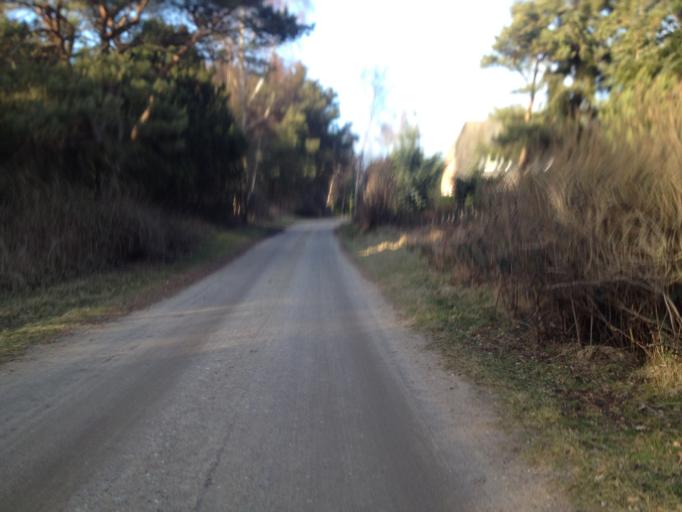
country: DE
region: Schleswig-Holstein
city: Nebel
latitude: 54.6444
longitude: 8.3475
